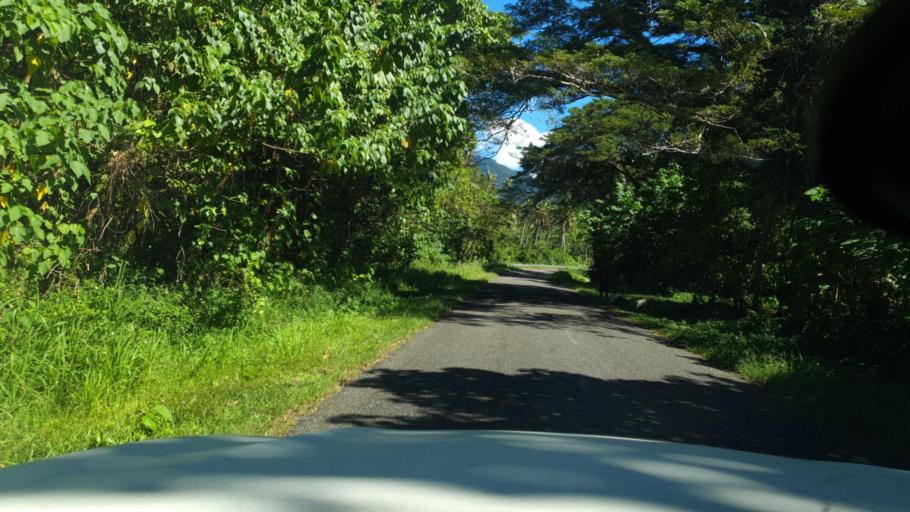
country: SB
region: Guadalcanal
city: Honiara
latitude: -9.2845
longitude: 159.7440
